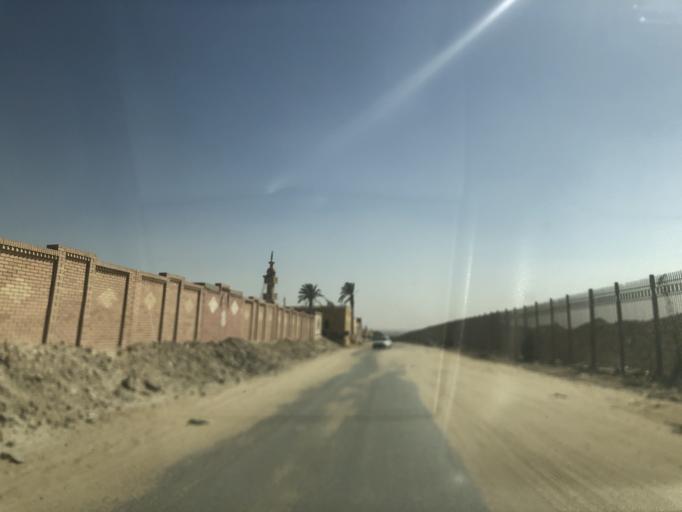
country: EG
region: Al Jizah
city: Madinat Sittah Uktubar
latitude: 29.9319
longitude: 30.9548
